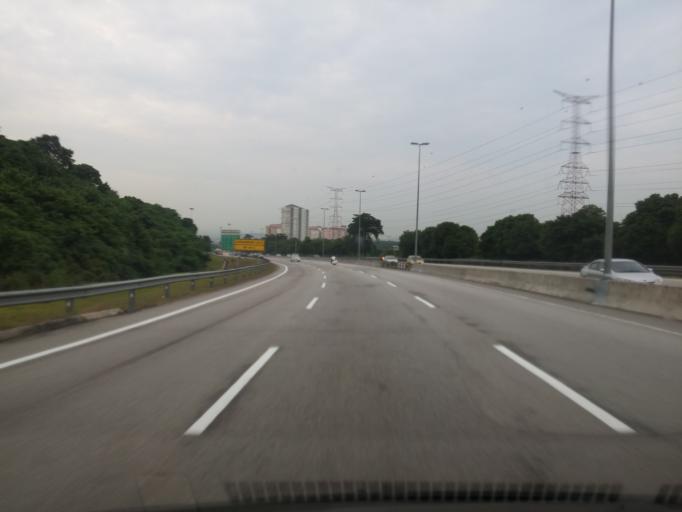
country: MY
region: Kuala Lumpur
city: Kuala Lumpur
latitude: 3.1028
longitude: 101.7045
